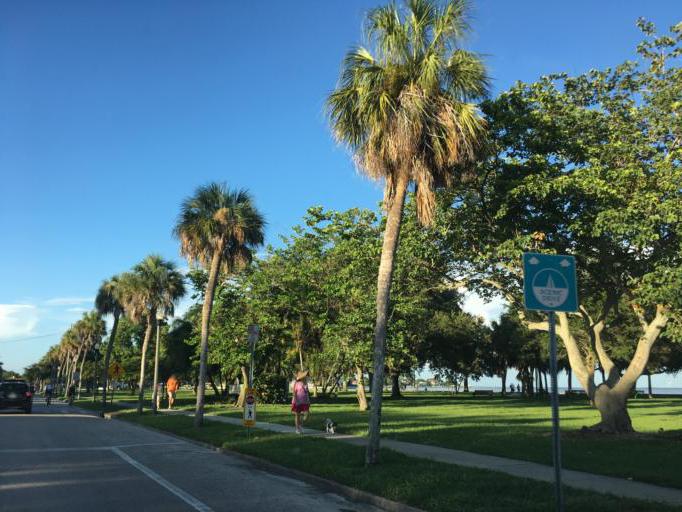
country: US
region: Florida
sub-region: Pinellas County
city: Saint Petersburg
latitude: 27.7863
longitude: -82.6242
